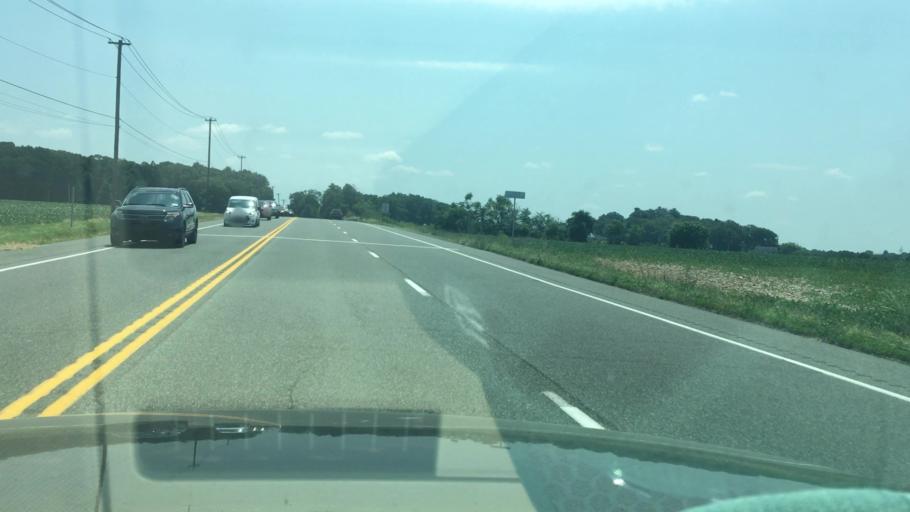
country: US
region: Pennsylvania
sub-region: Lehigh County
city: Schnecksville
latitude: 40.6197
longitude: -75.6615
